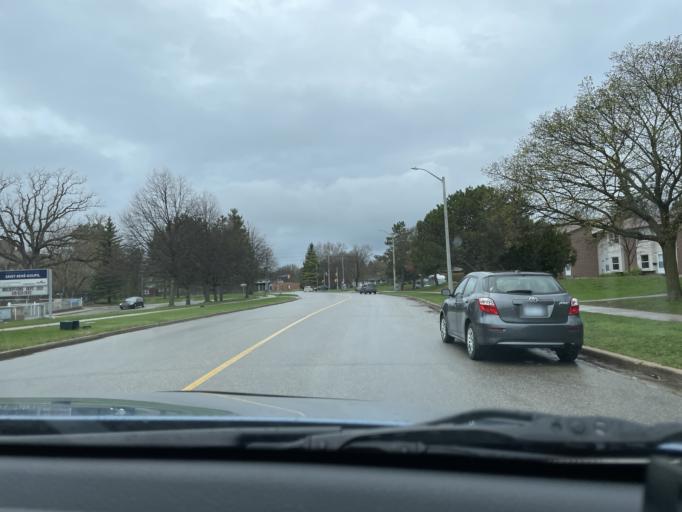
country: CA
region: Ontario
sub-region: Wellington County
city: Guelph
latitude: 43.5223
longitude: -80.2428
